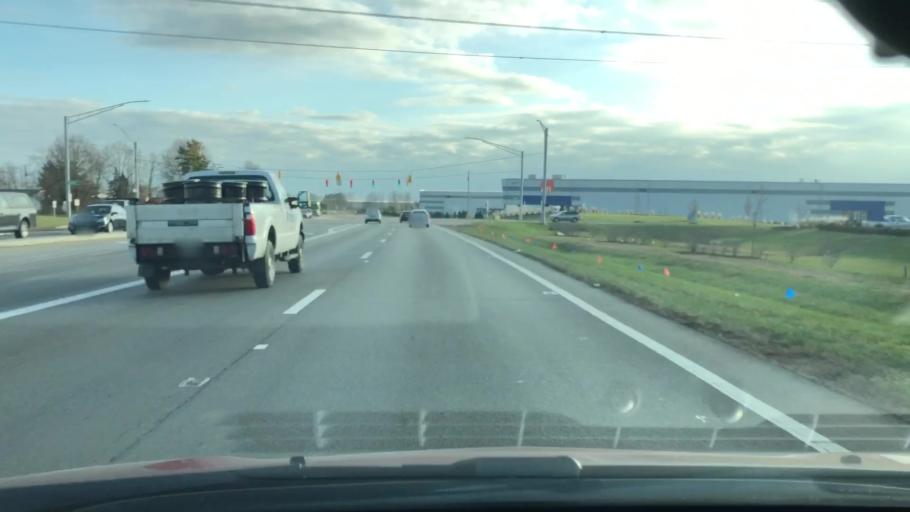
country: US
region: Ohio
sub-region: Franklin County
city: Obetz
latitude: 39.8501
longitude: -82.9386
